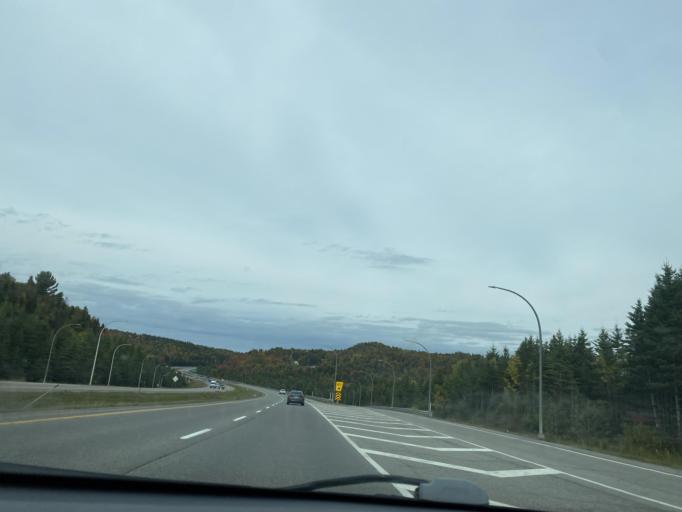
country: CA
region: Quebec
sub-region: Laurentides
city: Val-David
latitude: 46.0075
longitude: -74.2293
